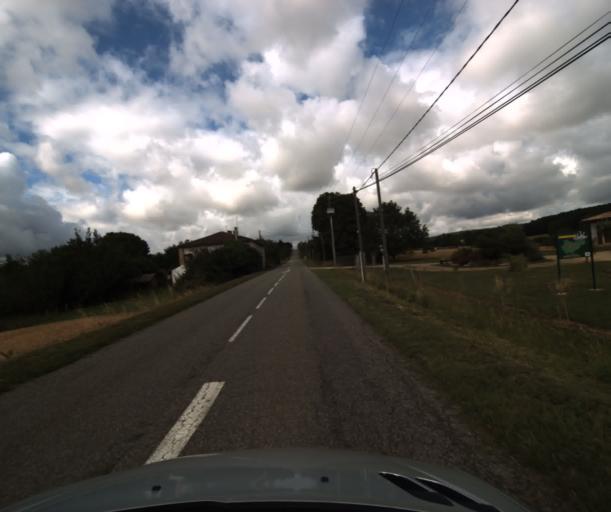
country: FR
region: Midi-Pyrenees
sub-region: Departement du Tarn-et-Garonne
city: Lavit
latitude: 43.9717
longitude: 0.9483
